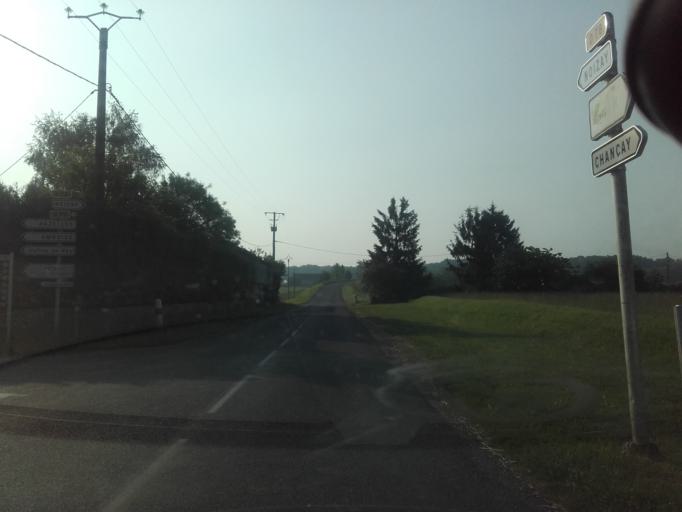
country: FR
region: Centre
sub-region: Departement d'Indre-et-Loire
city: Reugny
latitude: 47.4506
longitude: 0.8764
